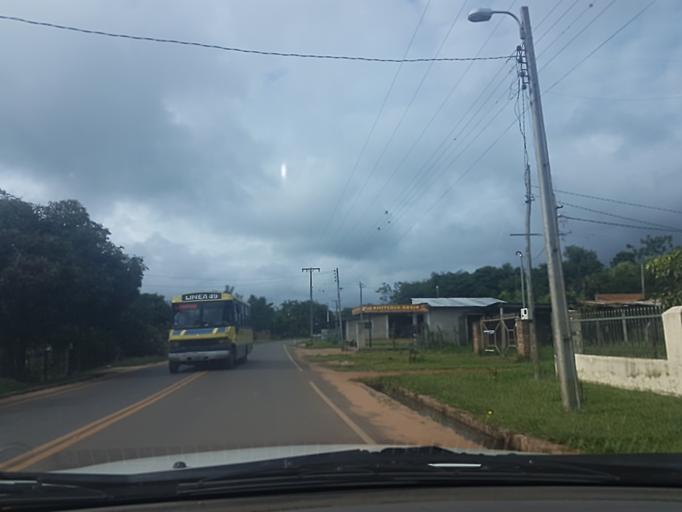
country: PY
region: Central
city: Limpio
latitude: -25.2332
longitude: -57.4494
